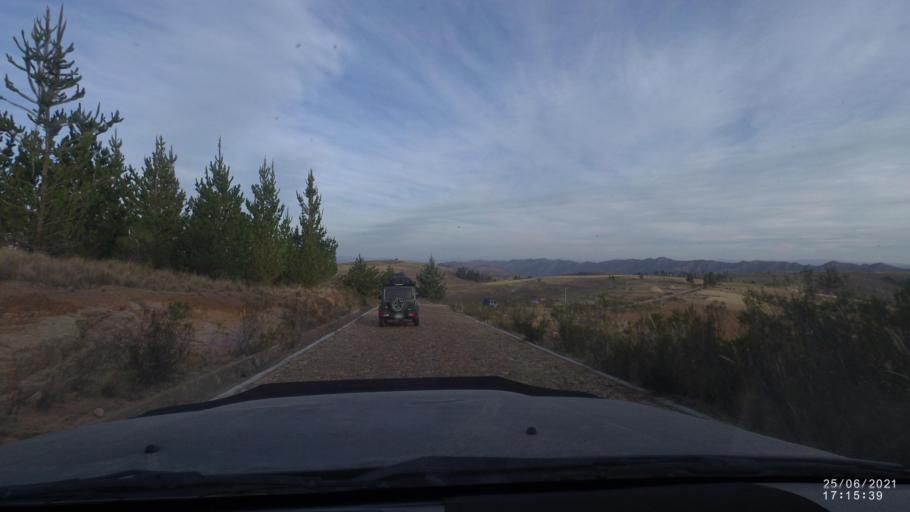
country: BO
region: Cochabamba
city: Arani
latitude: -17.8752
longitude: -65.6987
